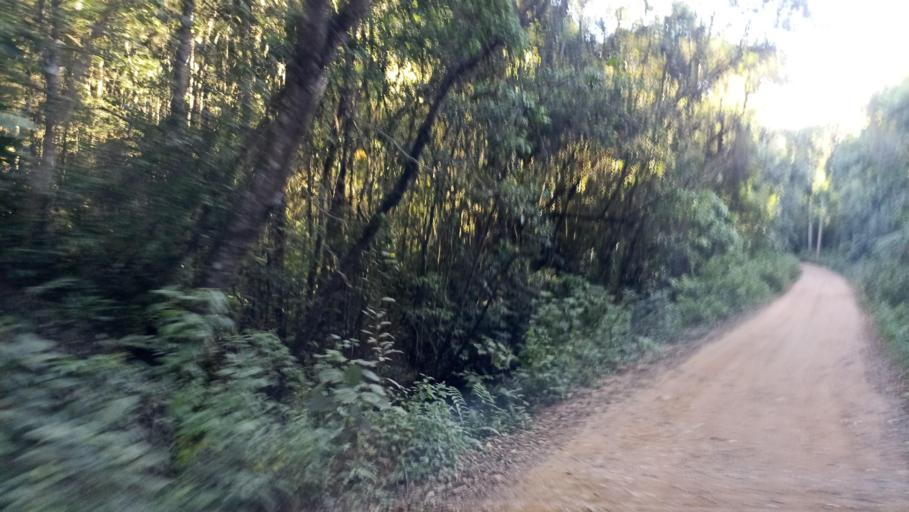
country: BR
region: Minas Gerais
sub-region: Ouro Preto
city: Ouro Preto
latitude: -20.2955
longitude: -43.5733
